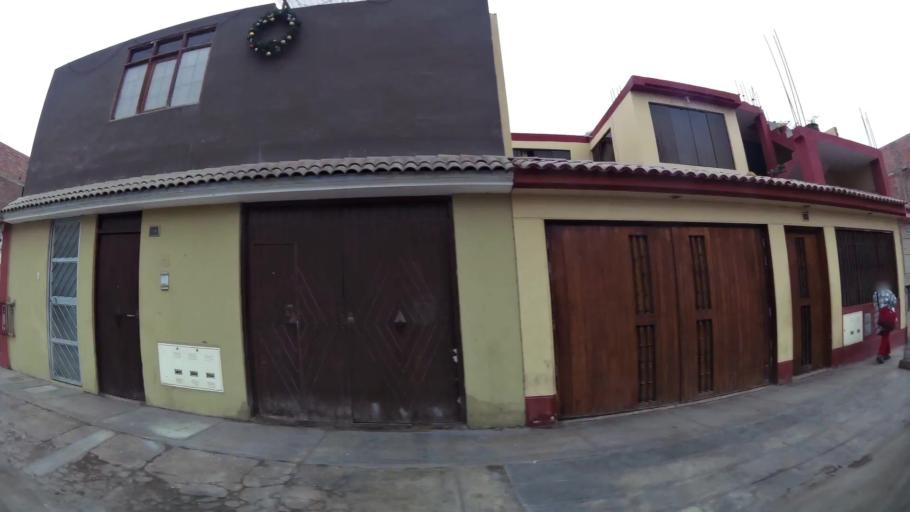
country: PE
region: Callao
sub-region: Callao
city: Callao
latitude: -12.0573
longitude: -77.1254
